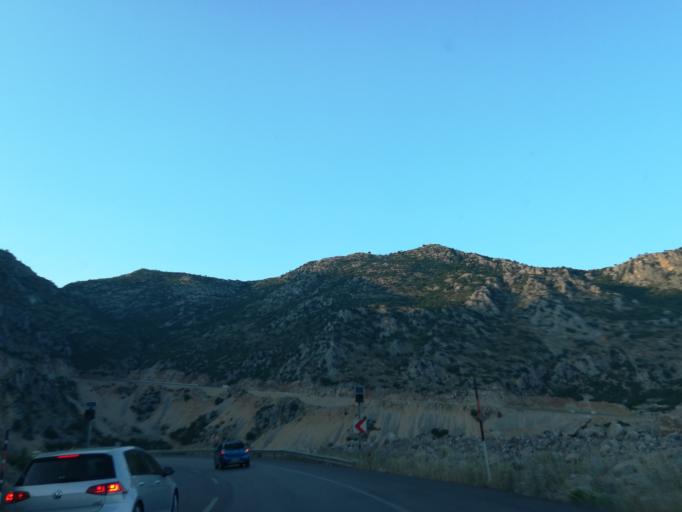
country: TR
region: Antalya
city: Dagbeli
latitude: 37.1553
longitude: 30.5064
